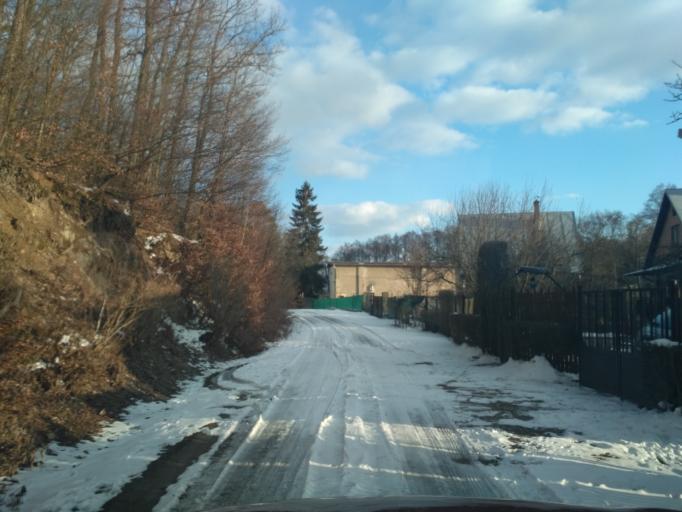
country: SK
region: Kosicky
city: Kosice
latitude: 48.7358
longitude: 21.1575
